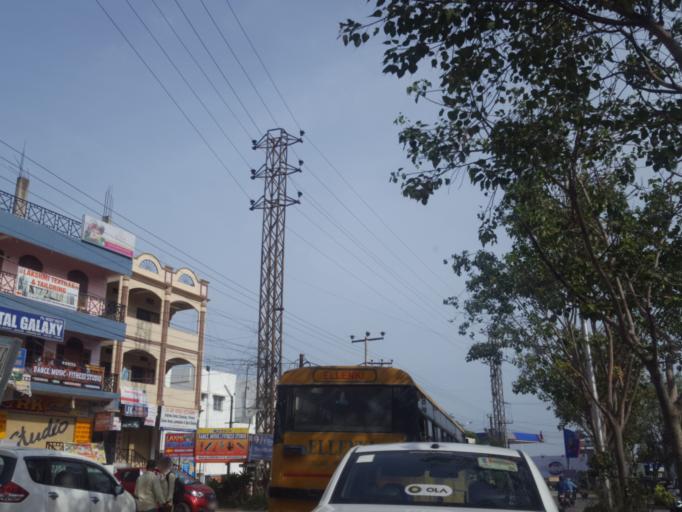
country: IN
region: Telangana
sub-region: Medak
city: Serilingampalle
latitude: 17.4780
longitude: 78.3200
